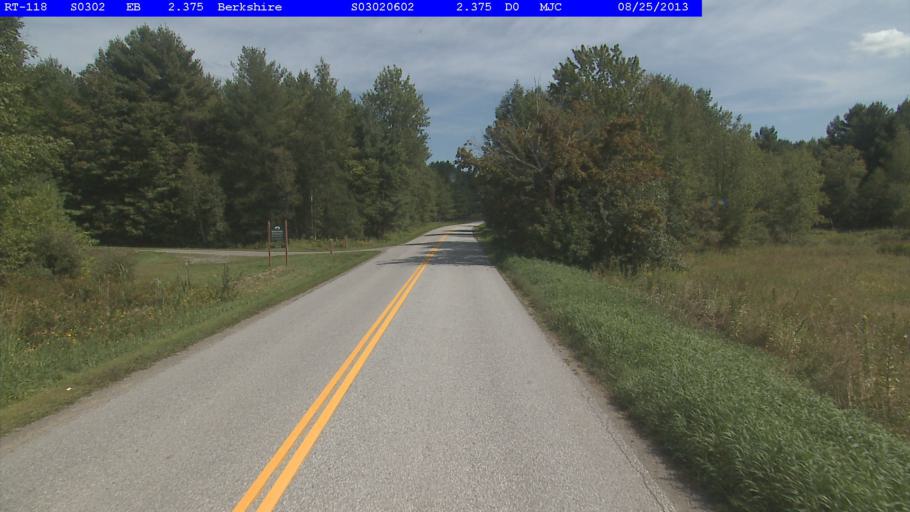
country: US
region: Vermont
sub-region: Franklin County
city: Enosburg Falls
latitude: 44.9756
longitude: -72.7703
